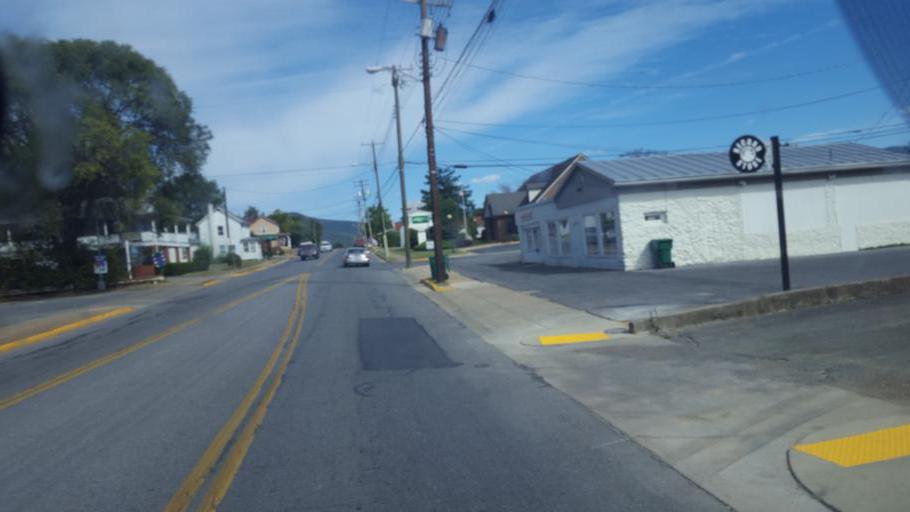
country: US
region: Virginia
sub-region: Page County
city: Luray
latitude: 38.6659
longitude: -78.4468
